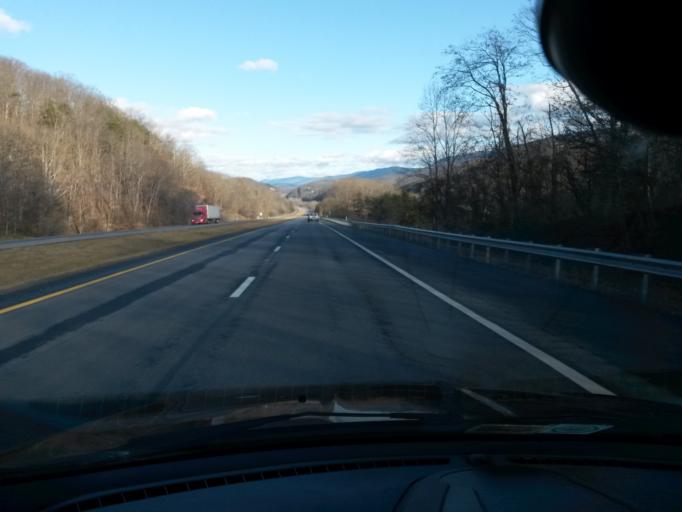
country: US
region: West Virginia
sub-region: Mercer County
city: Athens
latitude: 37.3449
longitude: -80.9333
